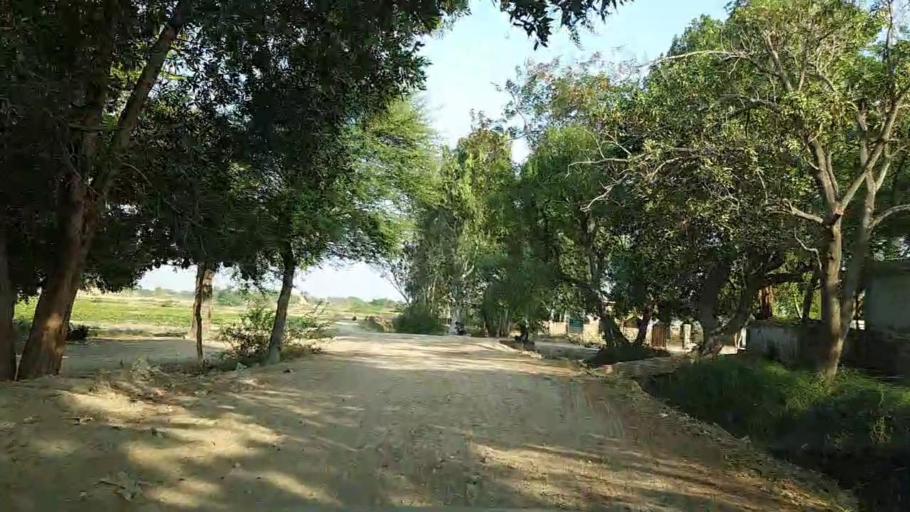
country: PK
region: Sindh
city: Mirpur Sakro
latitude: 24.5999
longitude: 67.6557
